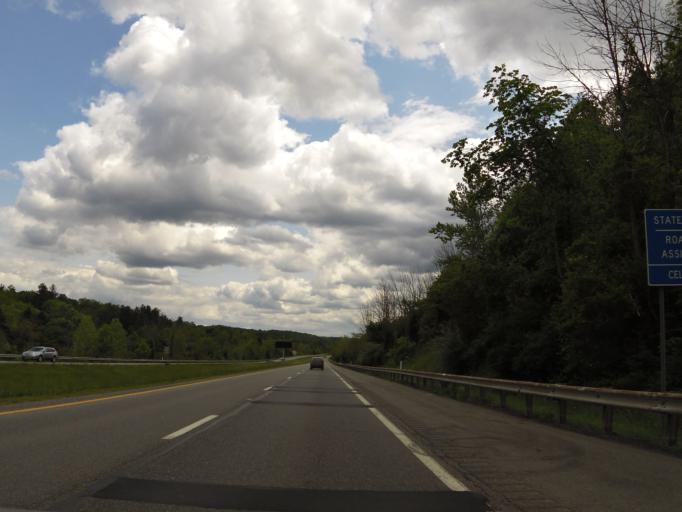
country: US
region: West Virginia
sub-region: Jackson County
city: Ripley
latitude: 38.7386
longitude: -81.6705
